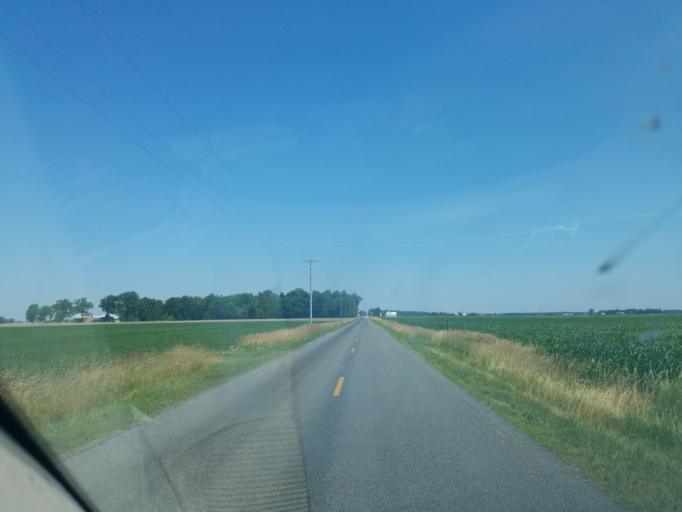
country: US
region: Ohio
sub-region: Mercer County
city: Rockford
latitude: 40.6510
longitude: -84.7086
